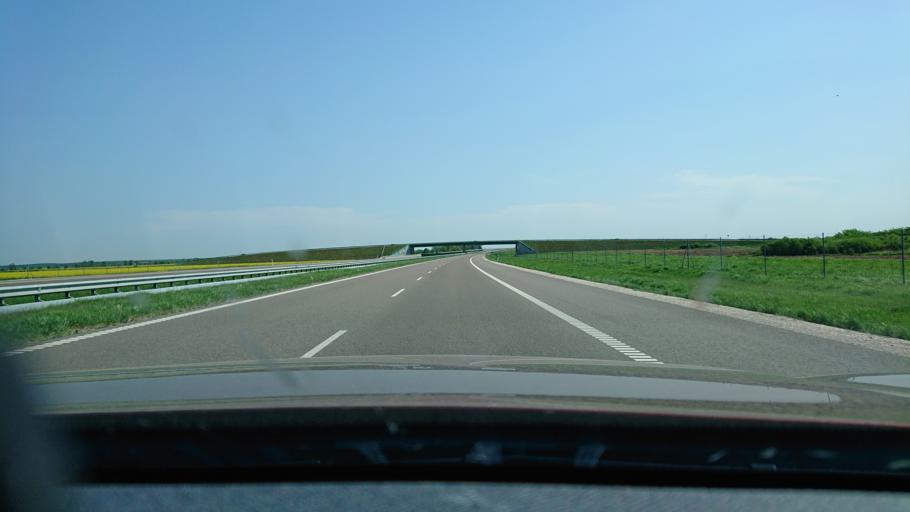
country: PL
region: Subcarpathian Voivodeship
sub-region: Powiat jaroslawski
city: Sosnica
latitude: 49.9257
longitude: 22.8965
